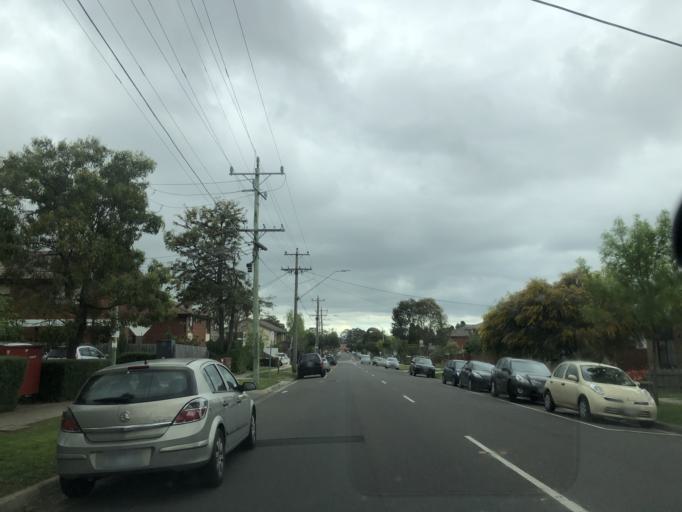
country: AU
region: Victoria
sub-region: Greater Dandenong
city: Dandenong
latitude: -37.9818
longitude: 145.2062
